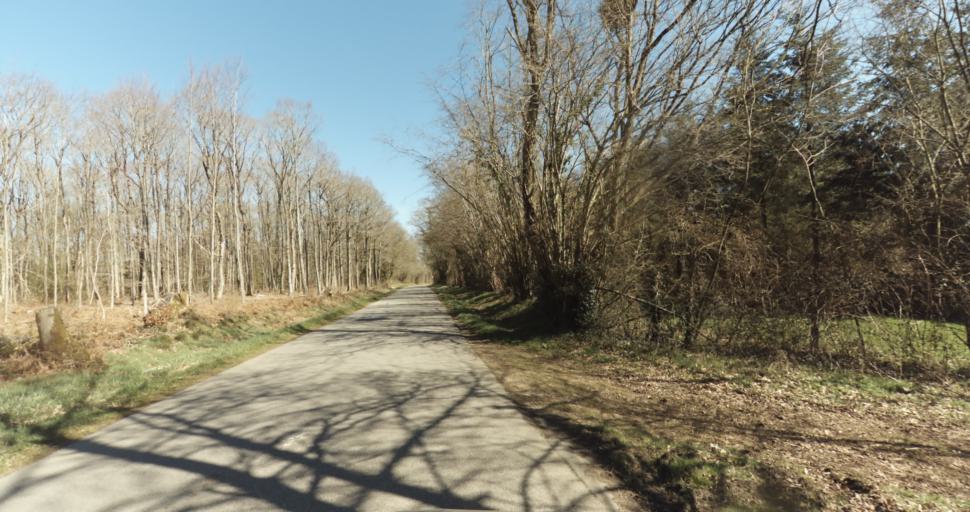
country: FR
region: Lower Normandy
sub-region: Departement du Calvados
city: Livarot
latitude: 48.9707
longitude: 0.1013
